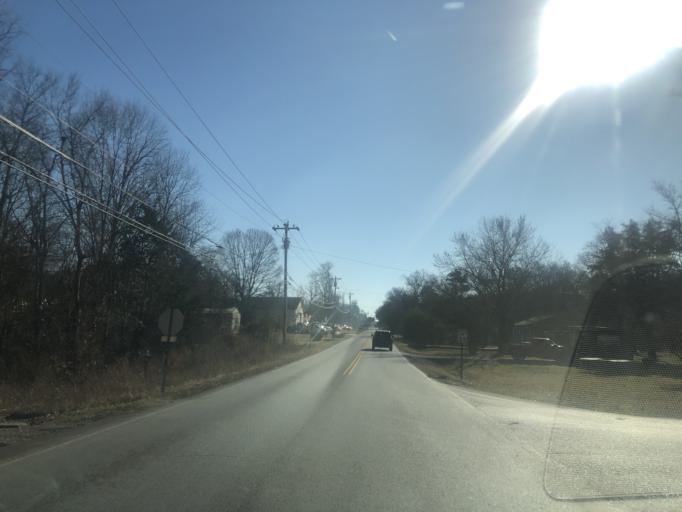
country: US
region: Tennessee
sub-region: Rutherford County
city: La Vergne
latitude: 36.0009
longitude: -86.5616
